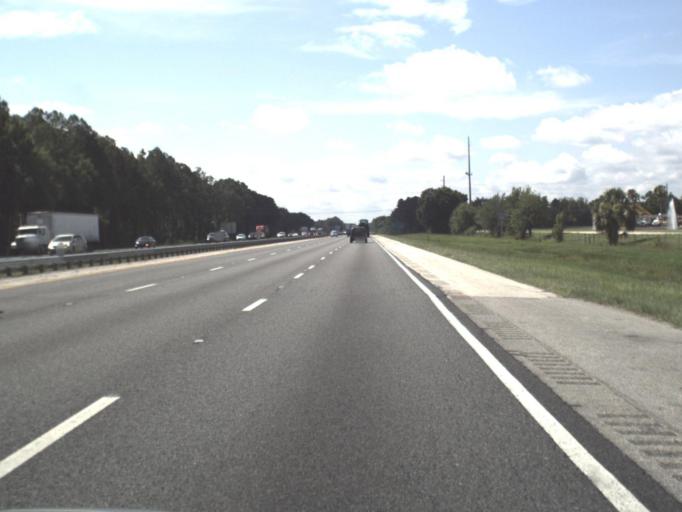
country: US
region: Florida
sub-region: Saint Johns County
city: Villano Beach
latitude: 29.9787
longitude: -81.4575
